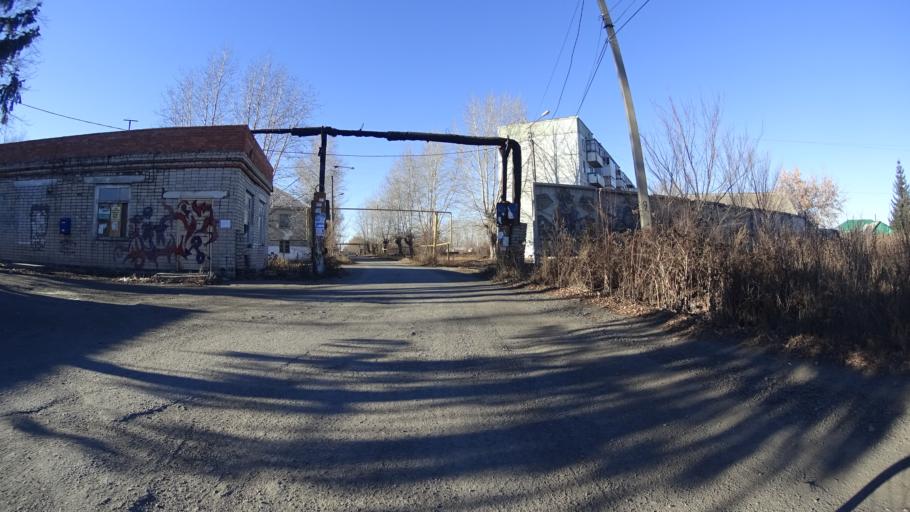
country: RU
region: Chelyabinsk
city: Troitsk
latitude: 54.1075
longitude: 61.5562
